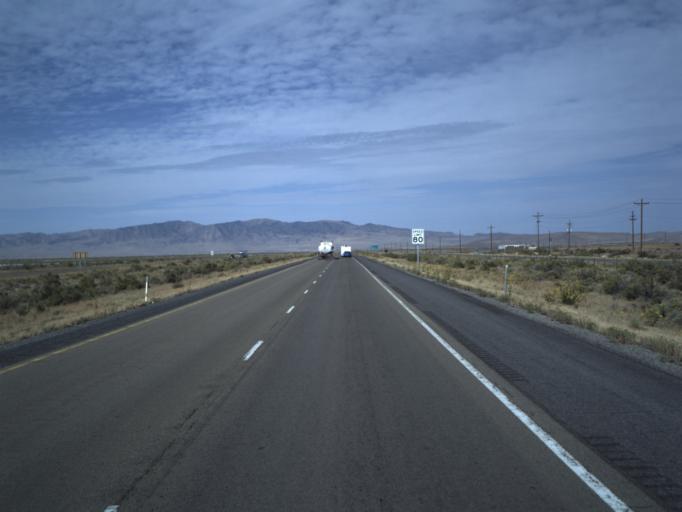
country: US
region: Utah
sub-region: Tooele County
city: Grantsville
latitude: 40.7474
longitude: -112.6660
